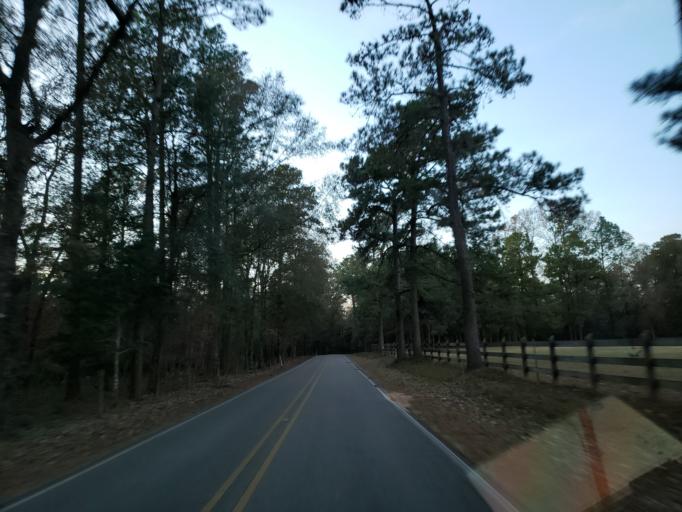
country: US
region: Mississippi
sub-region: Forrest County
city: Hattiesburg
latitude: 31.2421
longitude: -89.3154
